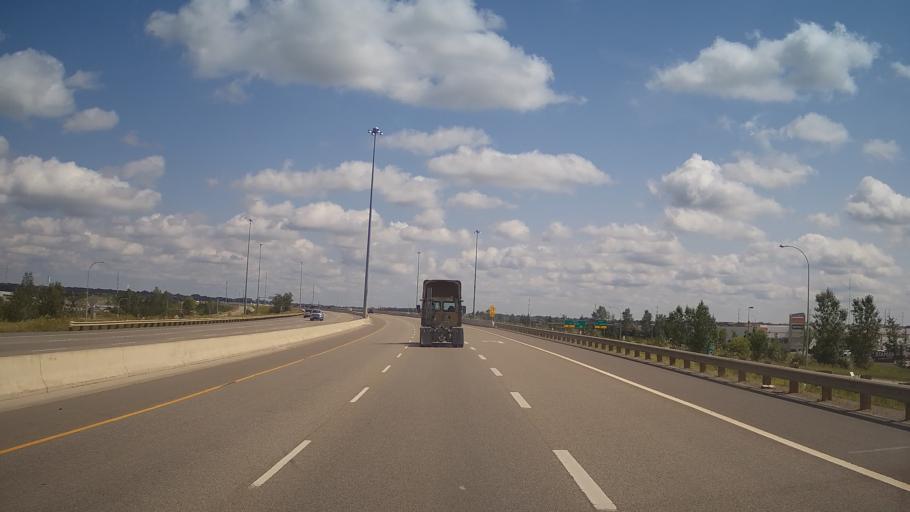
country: CA
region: Alberta
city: Sherwood Park
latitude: 53.4823
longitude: -113.3736
